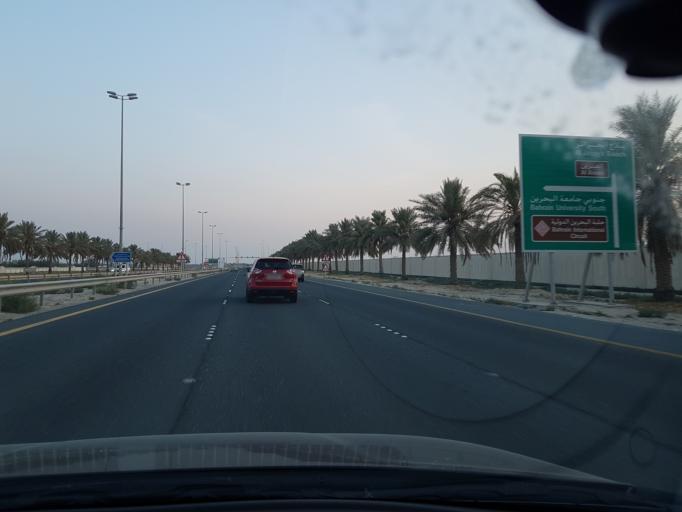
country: BH
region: Central Governorate
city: Dar Kulayb
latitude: 26.0417
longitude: 50.4998
